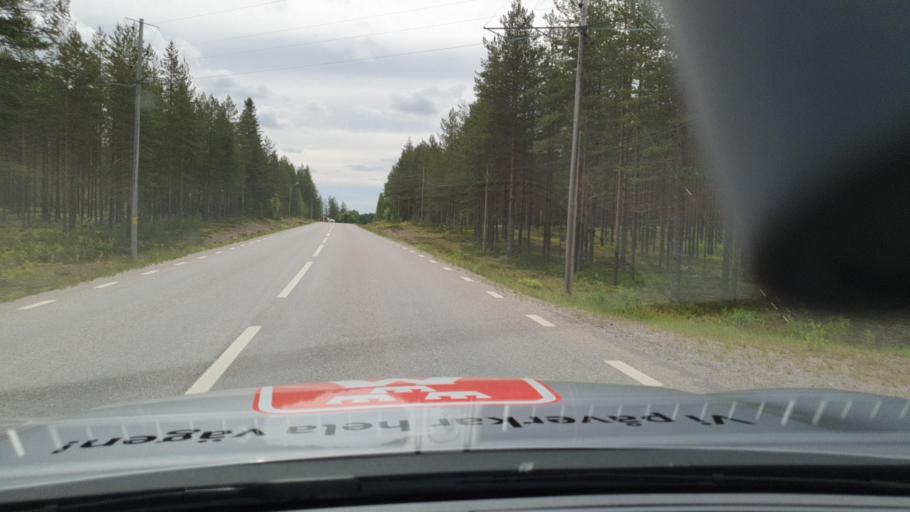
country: SE
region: Norrbotten
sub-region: Kalix Kommun
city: Kalix
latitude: 65.9539
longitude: 23.4528
